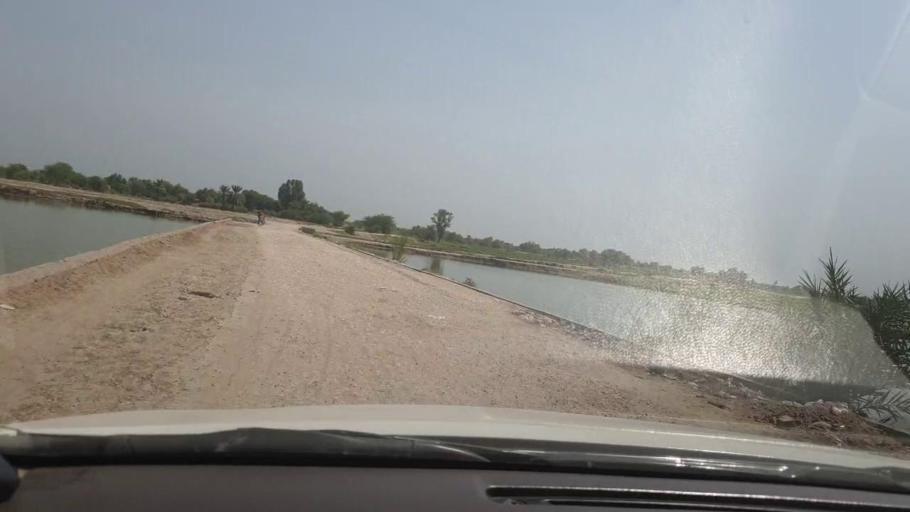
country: PK
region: Sindh
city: Shikarpur
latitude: 27.9324
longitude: 68.6033
